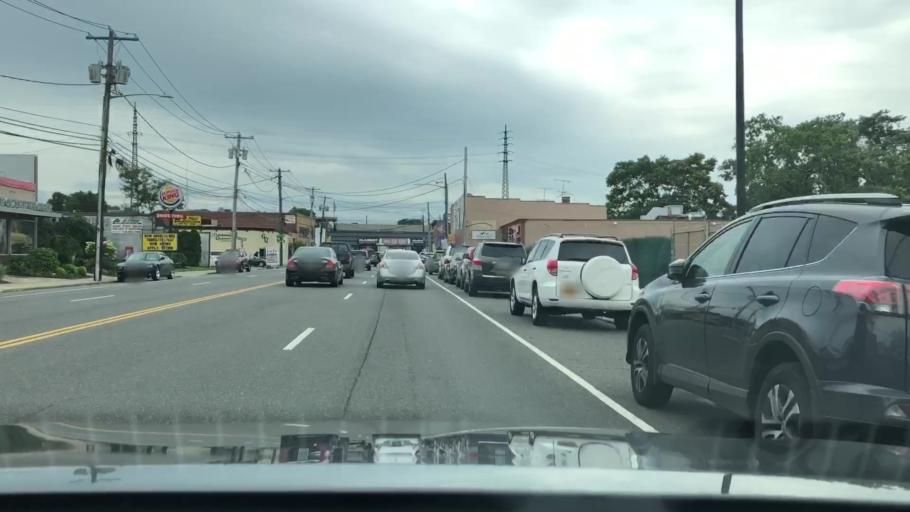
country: US
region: New York
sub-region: Nassau County
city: Baldwin
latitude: 40.6584
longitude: -73.6086
